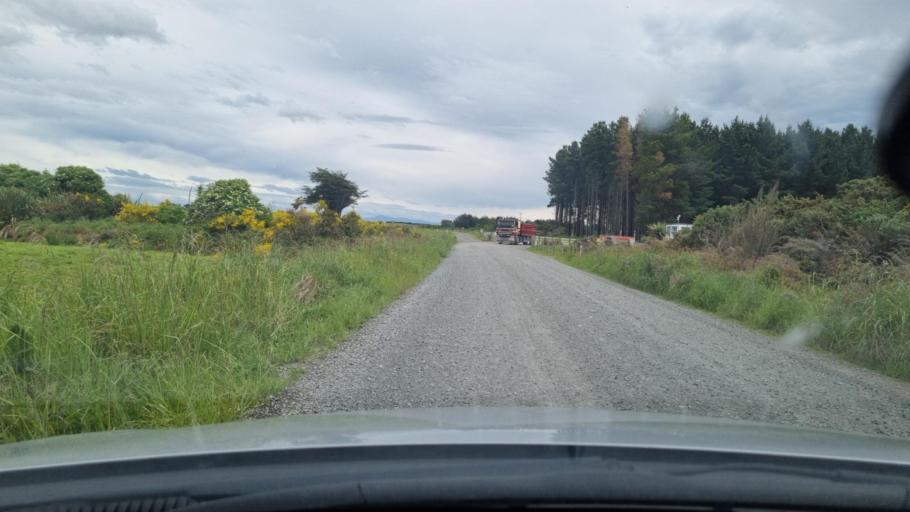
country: NZ
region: Southland
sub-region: Invercargill City
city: Invercargill
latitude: -46.4072
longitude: 168.2750
